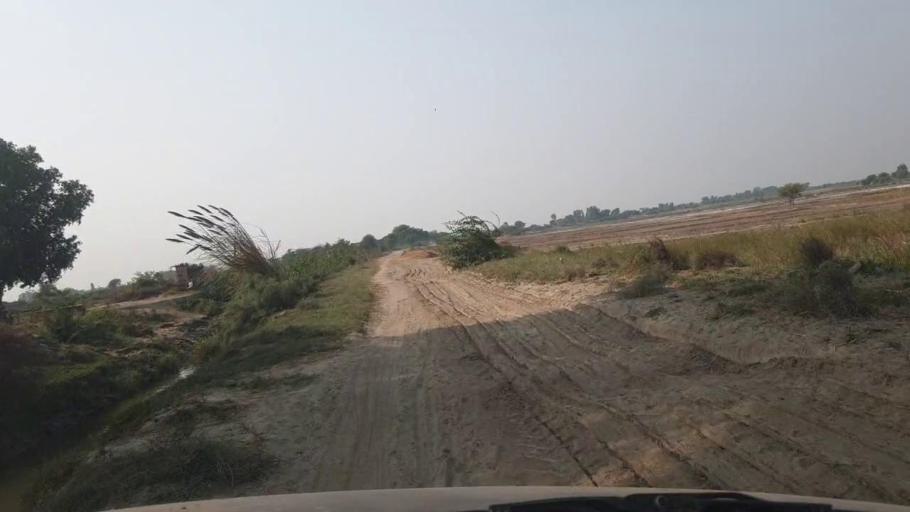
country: PK
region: Sindh
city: Tando Muhammad Khan
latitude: 25.0772
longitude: 68.3499
